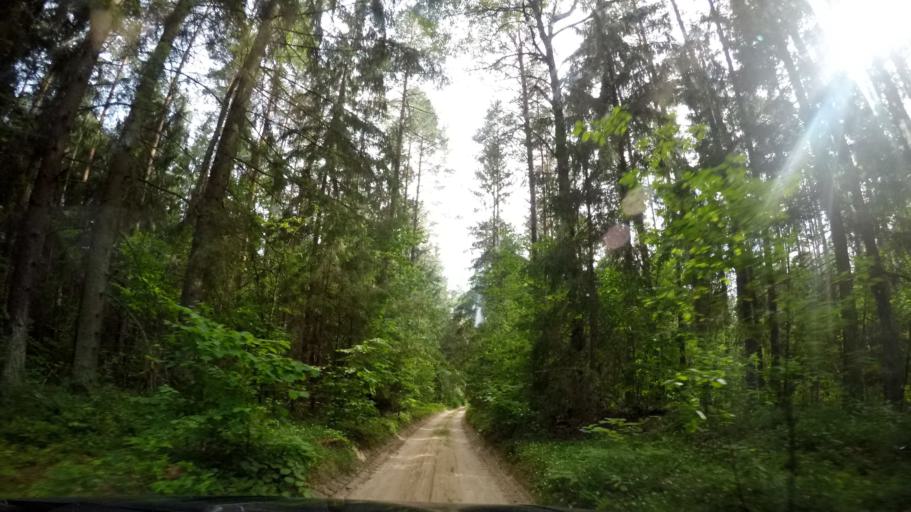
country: BY
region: Grodnenskaya
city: Skidal'
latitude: 53.8344
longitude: 24.1769
